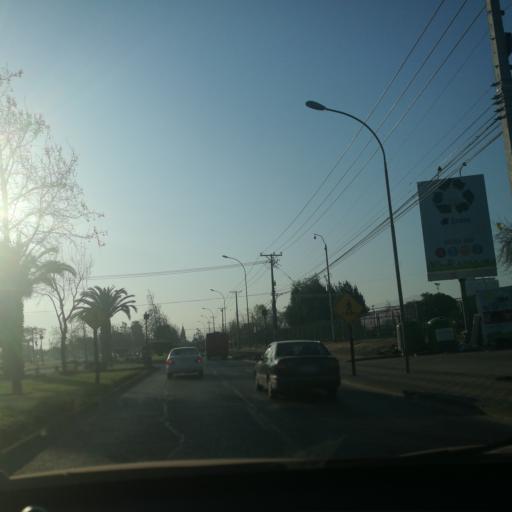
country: CL
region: O'Higgins
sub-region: Provincia de Cachapoal
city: Rancagua
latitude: -34.1683
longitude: -70.7211
